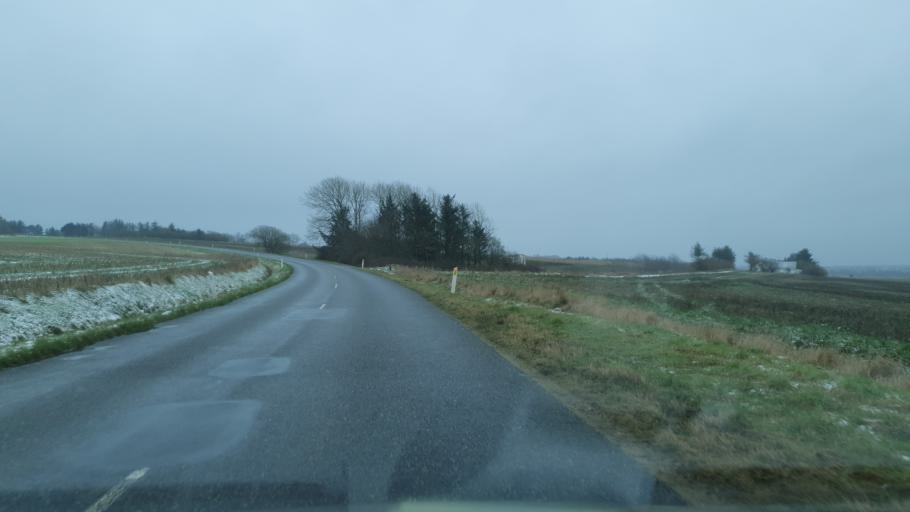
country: DK
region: North Denmark
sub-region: Jammerbugt Kommune
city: Brovst
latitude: 57.1284
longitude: 9.4732
